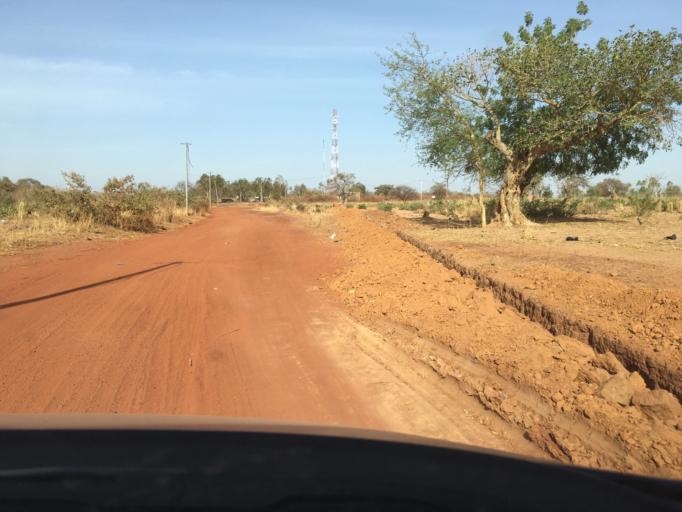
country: BF
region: Plateau-Central
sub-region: Province du Kourweogo
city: Bousse
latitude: 12.5577
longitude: -1.8955
